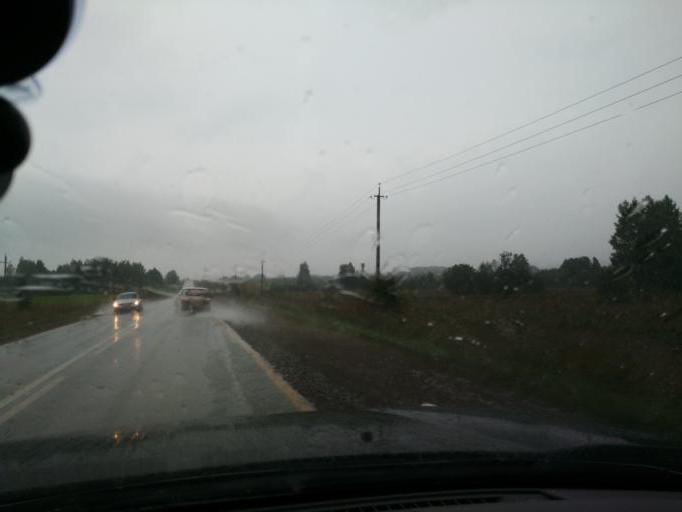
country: RU
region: Perm
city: Osa
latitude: 57.1655
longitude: 55.5312
